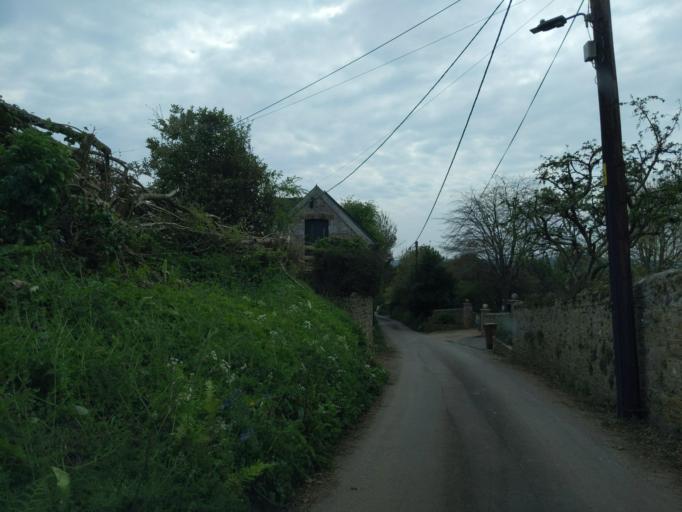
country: GB
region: England
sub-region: Devon
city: Yealmpton
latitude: 50.3523
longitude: -4.0410
